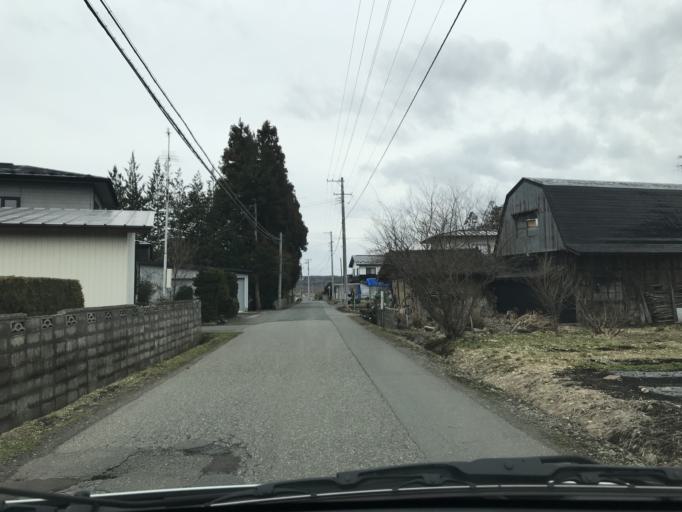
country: JP
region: Iwate
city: Kitakami
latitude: 39.2956
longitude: 141.0489
